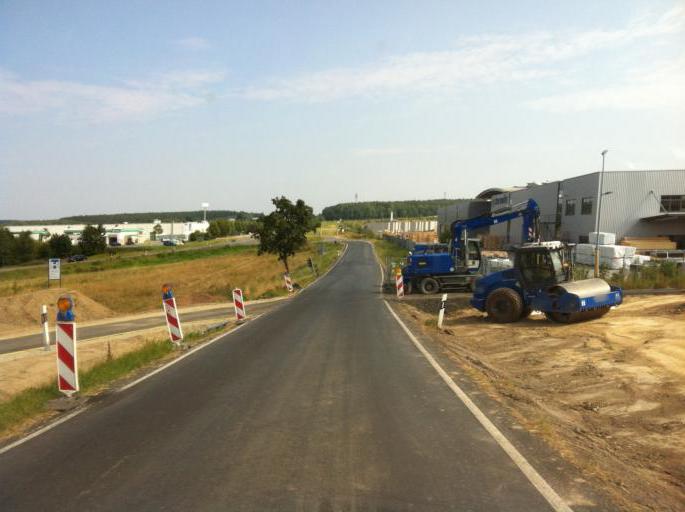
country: DE
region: Saxony
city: Reichenbach/Vogtland
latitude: 50.6028
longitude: 12.3158
